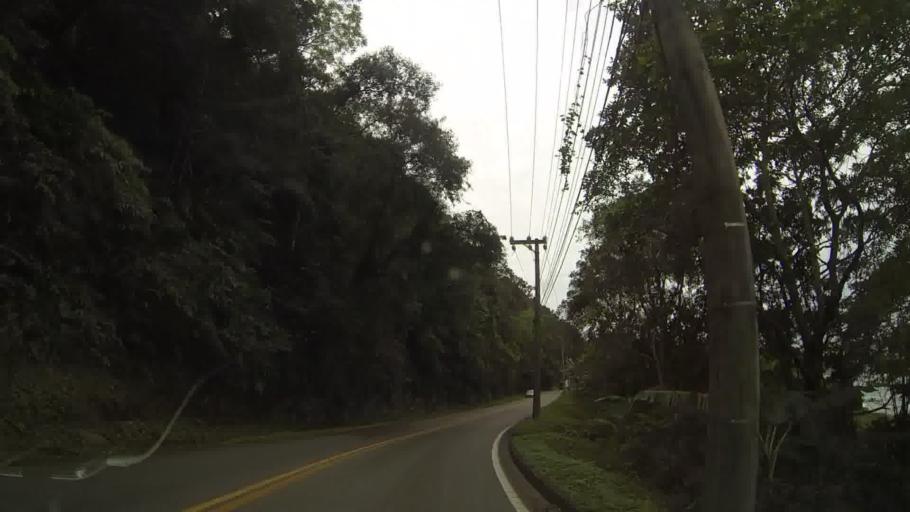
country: BR
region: Sao Paulo
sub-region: Sao Sebastiao
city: Sao Sebastiao
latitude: -23.8268
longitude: -45.5240
